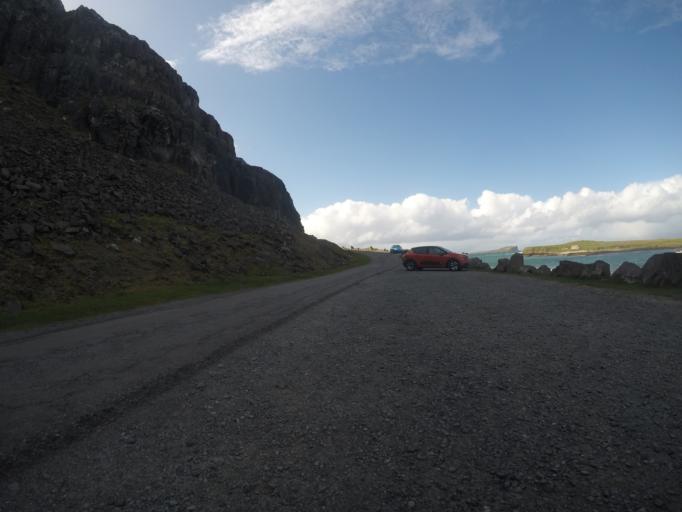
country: GB
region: Scotland
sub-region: Highland
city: Portree
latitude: 57.6361
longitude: -6.2048
